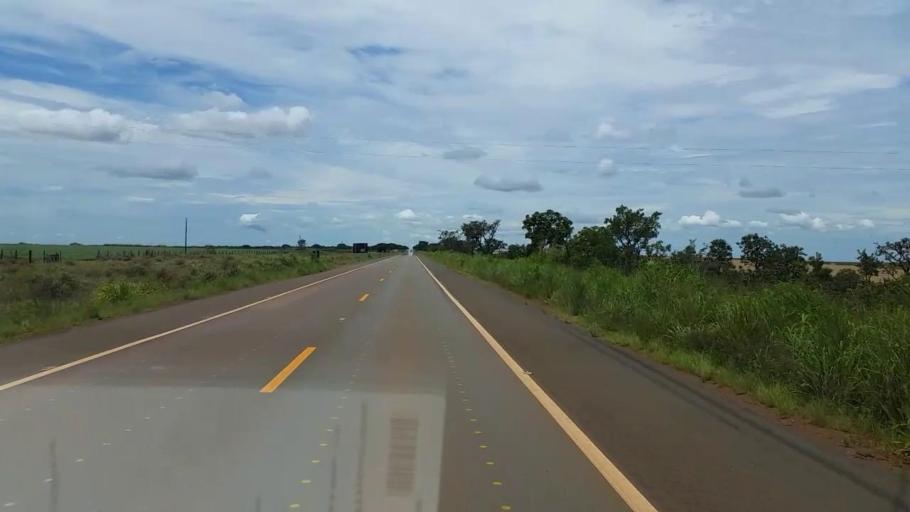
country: BR
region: Goias
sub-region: Luziania
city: Luziania
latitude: -16.1994
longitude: -47.4485
